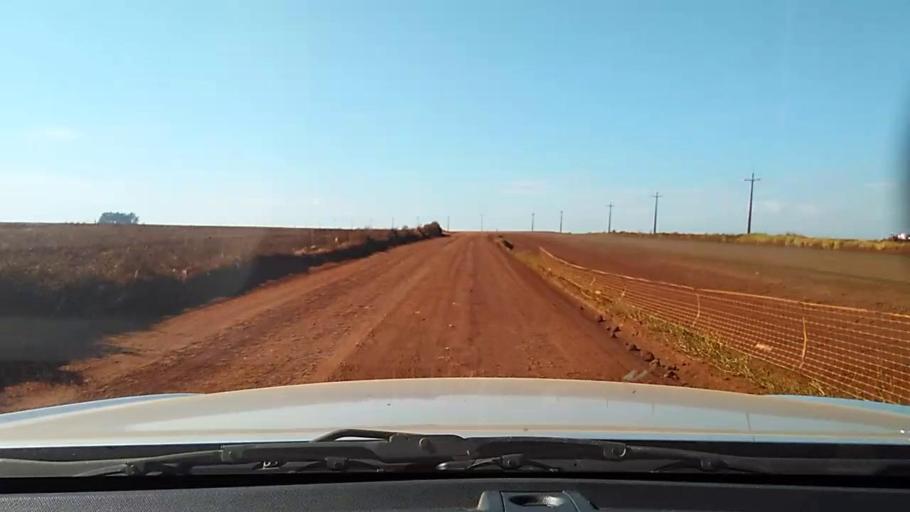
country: PY
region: Alto Parana
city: Naranjal
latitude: -25.9142
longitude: -55.4385
